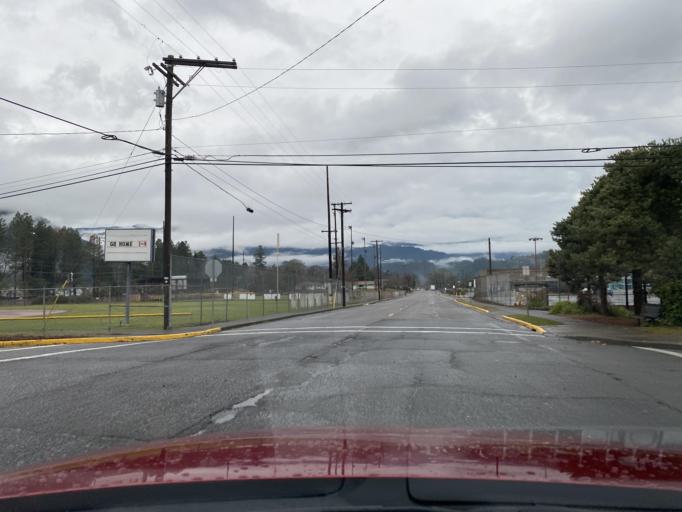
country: US
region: Oregon
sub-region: Lane County
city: Oakridge
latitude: 43.7481
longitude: -122.4671
